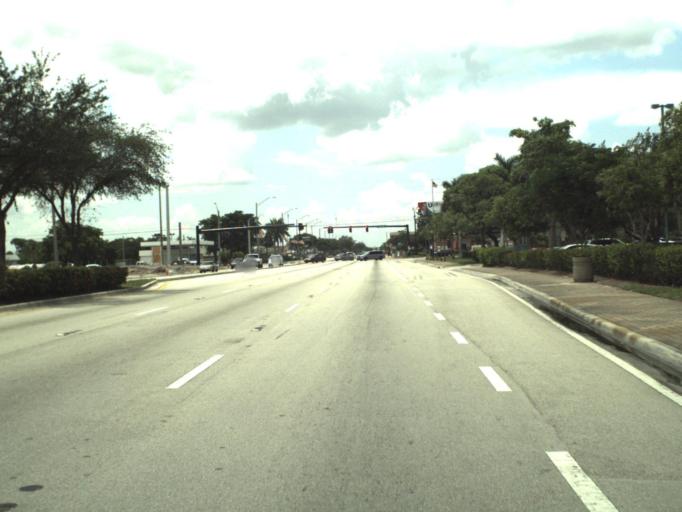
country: US
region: Florida
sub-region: Broward County
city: Boulevard Gardens
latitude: 26.1217
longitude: -80.1762
